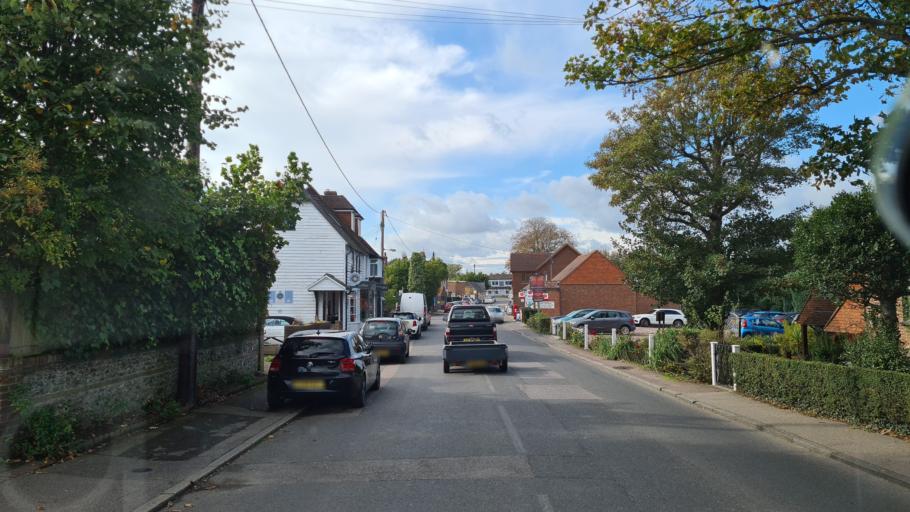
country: GB
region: England
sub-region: East Sussex
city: Bodle Street
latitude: 50.8894
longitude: 0.3259
